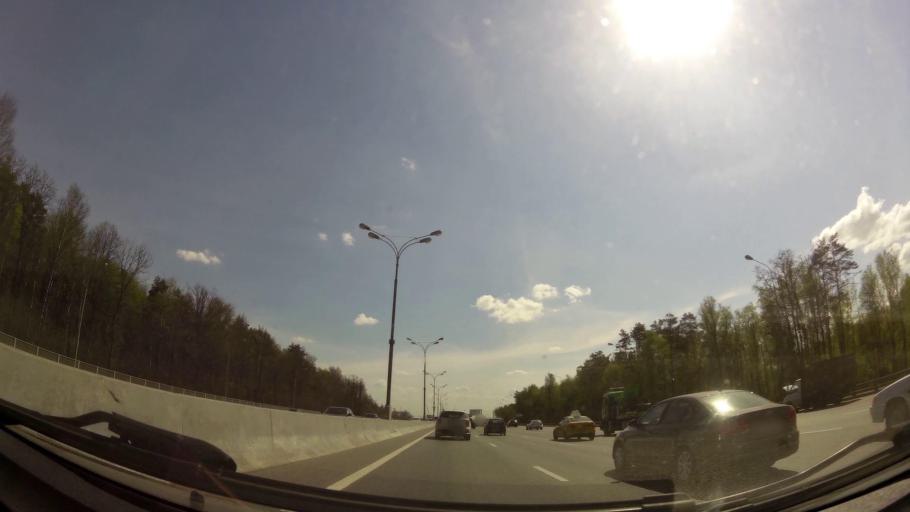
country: RU
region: Moskovskaya
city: Nemchinovka
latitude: 55.7397
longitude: 37.3725
